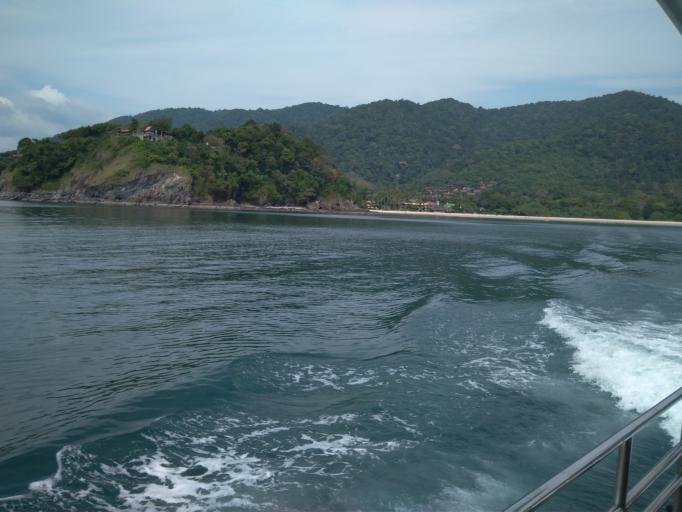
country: TH
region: Krabi
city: Ko Lanta
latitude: 7.4941
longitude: 99.0692
